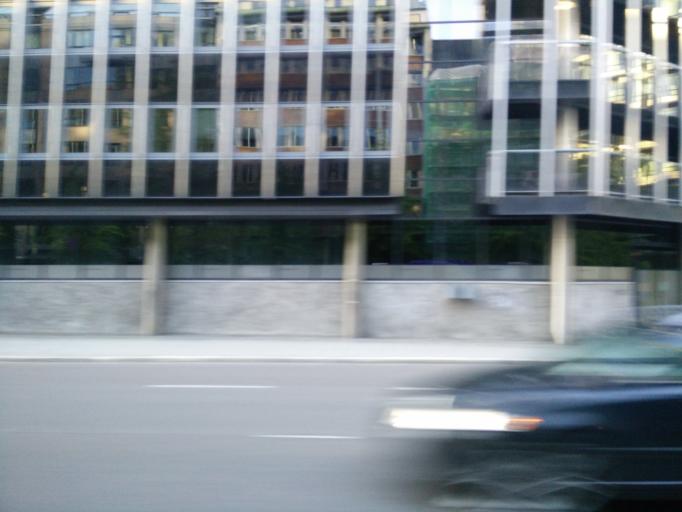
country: NO
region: Oslo
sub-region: Oslo
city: Oslo
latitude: 59.9168
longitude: 10.7404
